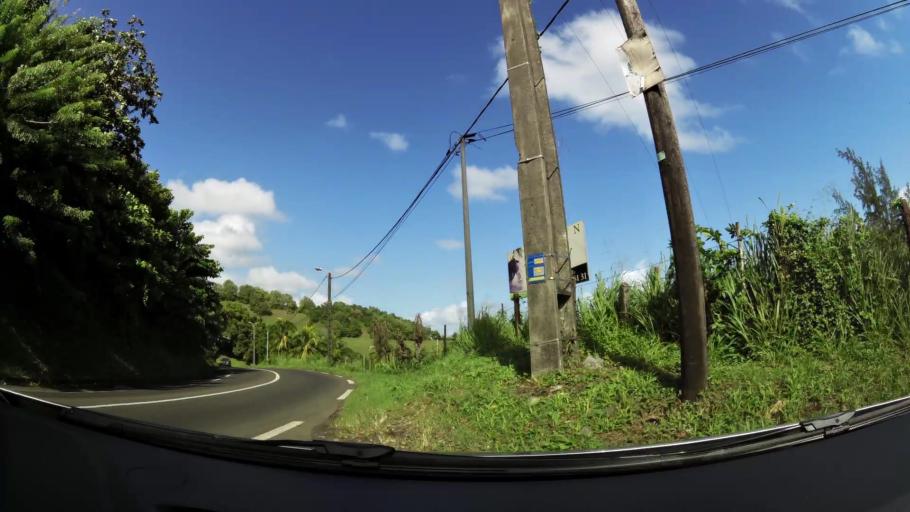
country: MQ
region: Martinique
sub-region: Martinique
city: Sainte-Marie
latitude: 14.7677
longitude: -60.9834
